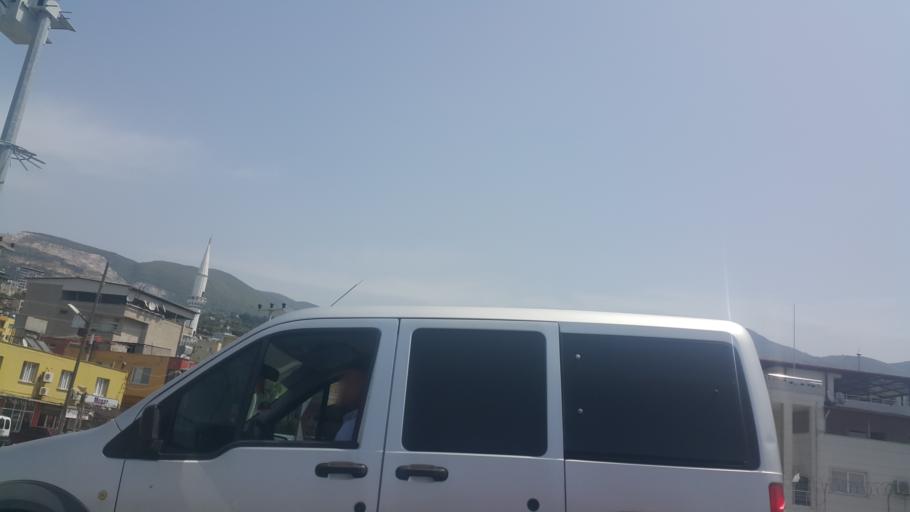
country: TR
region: Hatay
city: Denizciler
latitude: 36.6463
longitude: 36.2136
